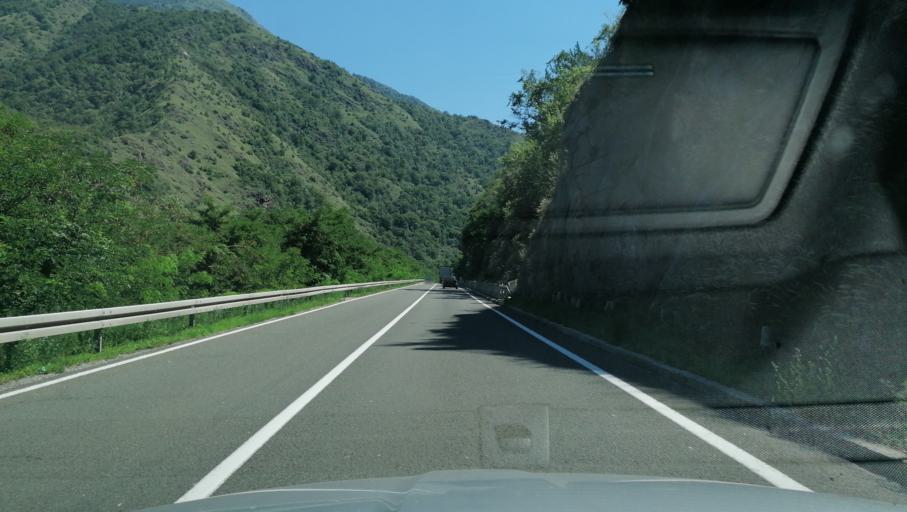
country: RS
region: Central Serbia
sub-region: Raski Okrug
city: Kraljevo
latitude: 43.5886
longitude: 20.5755
